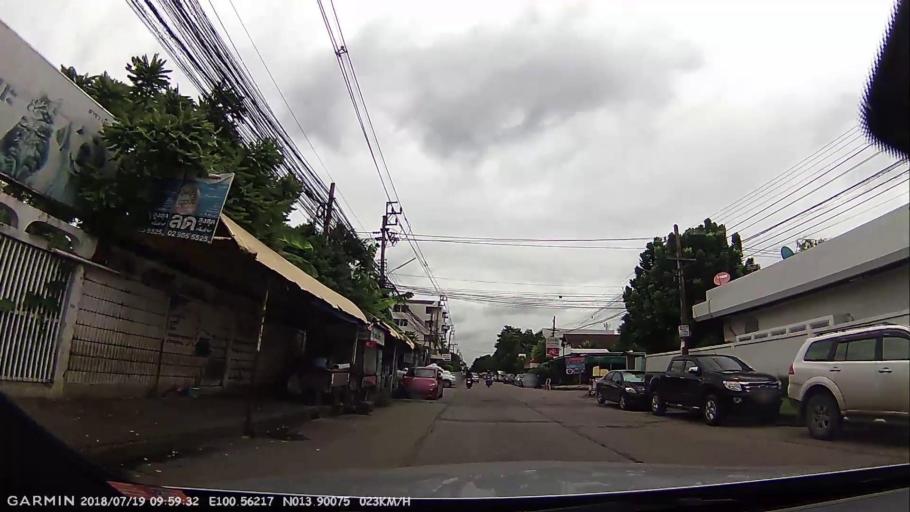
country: TH
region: Bangkok
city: Lak Si
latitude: 13.9008
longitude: 100.5622
